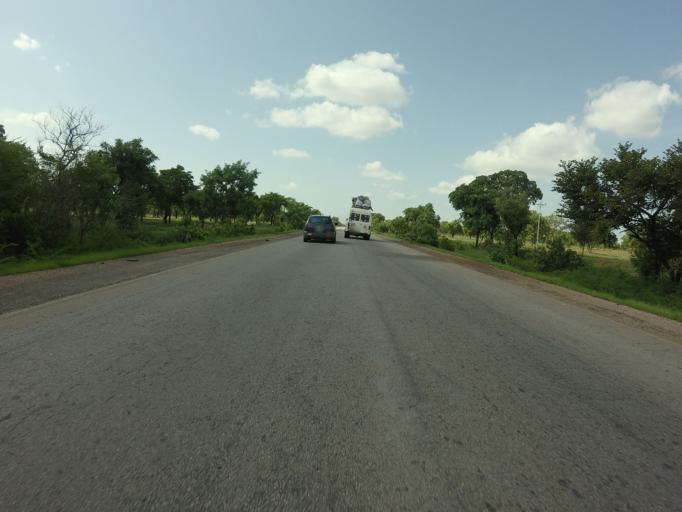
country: GH
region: Northern
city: Savelugu
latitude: 9.9455
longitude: -0.8388
